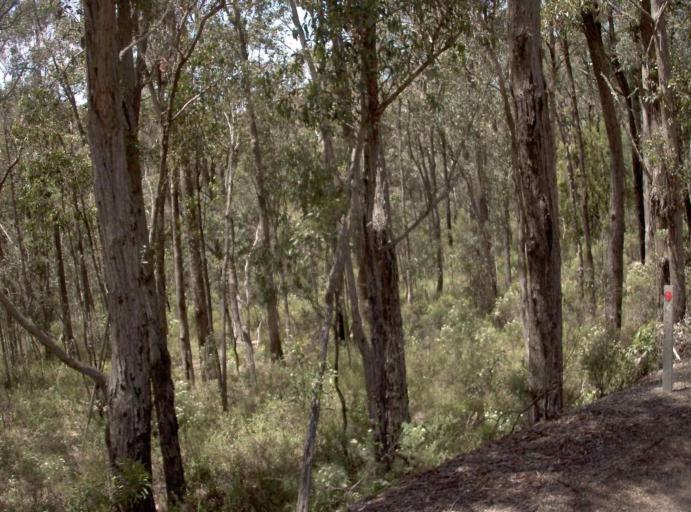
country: AU
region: Victoria
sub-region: East Gippsland
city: Lakes Entrance
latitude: -37.6253
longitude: 147.8843
